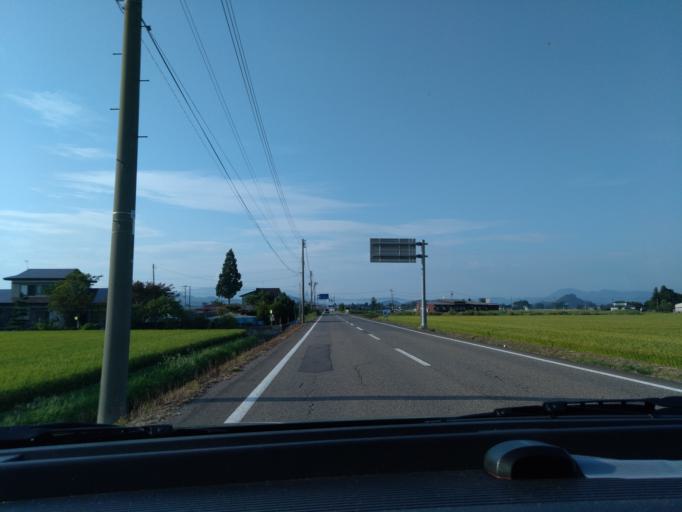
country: JP
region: Akita
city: Kakunodatemachi
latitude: 39.5465
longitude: 140.5577
